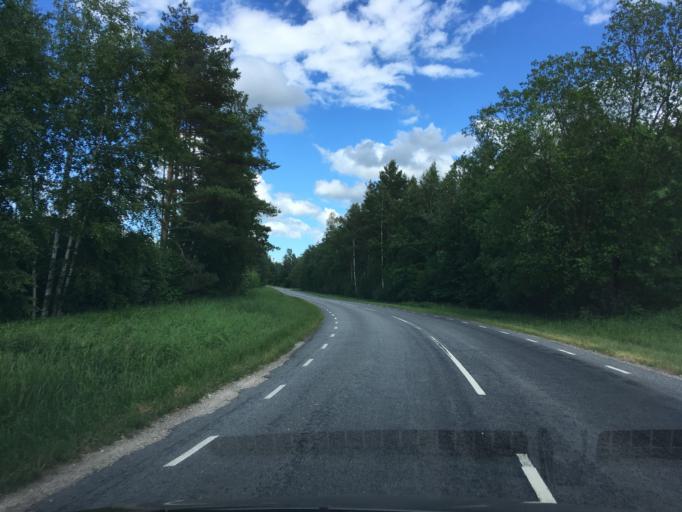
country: EE
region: Paernumaa
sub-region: Halinga vald
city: Parnu-Jaagupi
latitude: 58.6198
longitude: 24.4302
